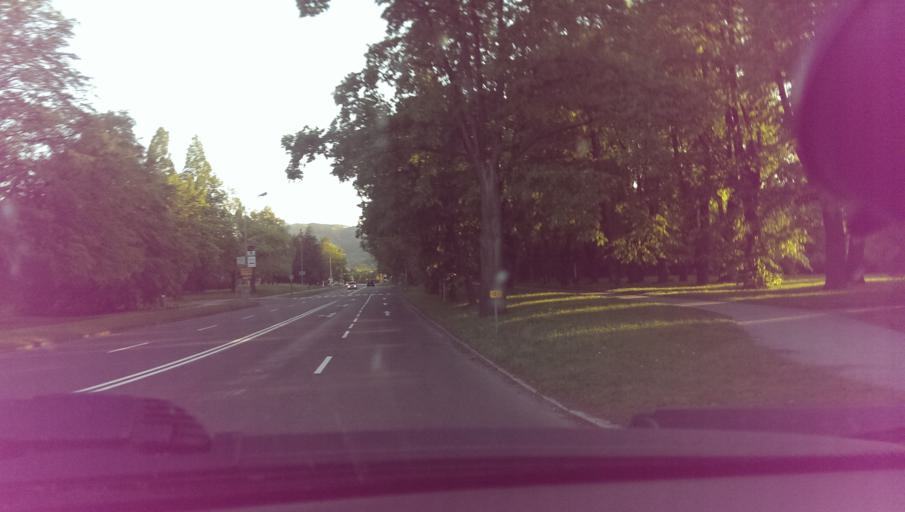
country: CZ
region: Moravskoslezsky
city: Frenstat pod Radhostem
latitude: 49.5440
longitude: 18.2096
